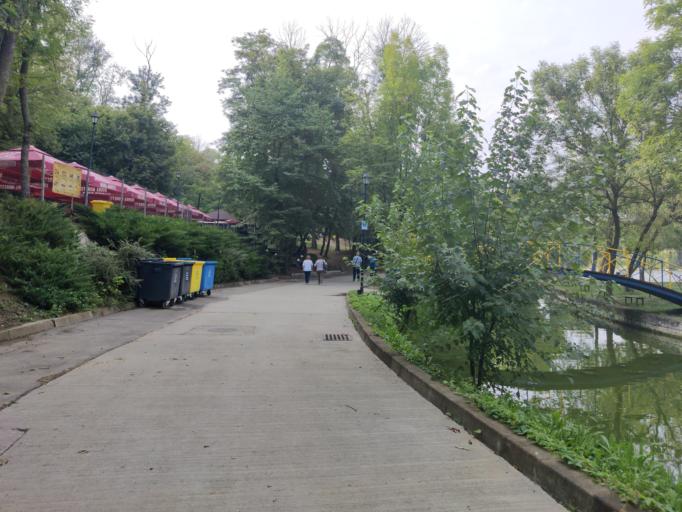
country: RO
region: Iasi
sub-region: Municipiul Iasi
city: Iasi
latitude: 47.1788
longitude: 27.6057
